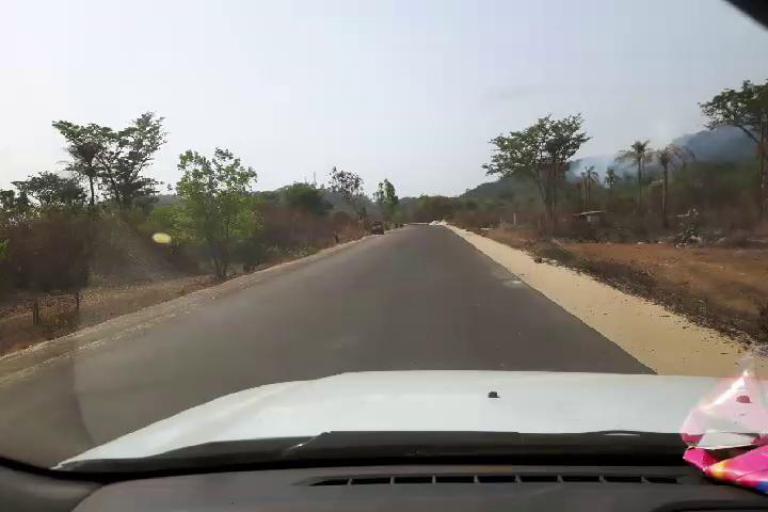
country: SL
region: Western Area
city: Waterloo
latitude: 8.2544
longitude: -13.1565
